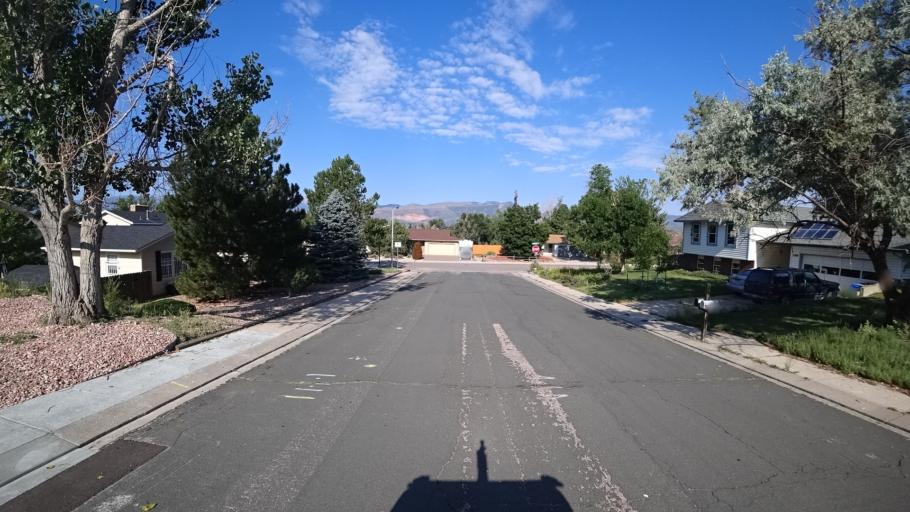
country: US
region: Colorado
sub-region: El Paso County
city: Air Force Academy
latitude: 38.9459
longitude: -104.7832
